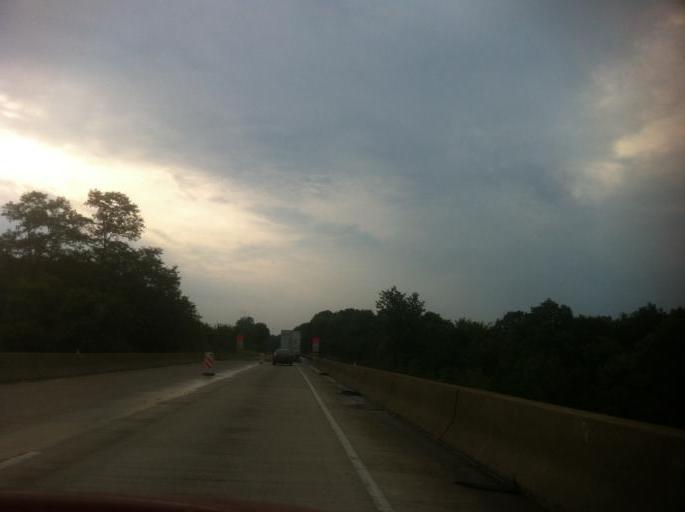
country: US
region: Pennsylvania
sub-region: Clarion County
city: Knox
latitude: 41.1897
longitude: -79.5620
